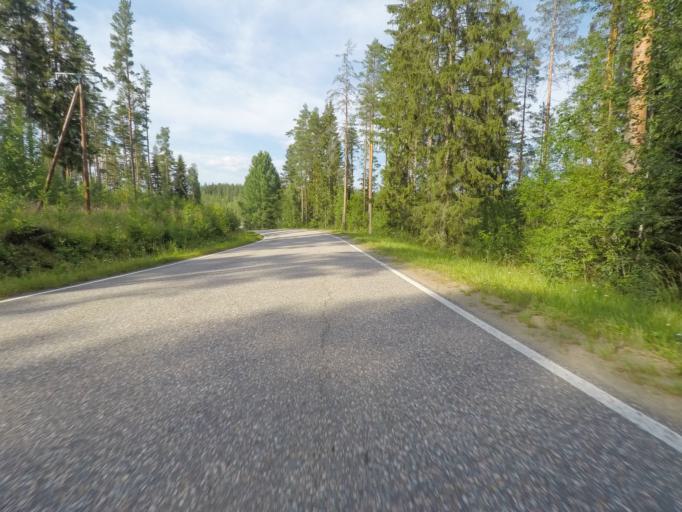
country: FI
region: Southern Savonia
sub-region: Savonlinna
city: Sulkava
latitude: 61.7809
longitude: 28.2397
